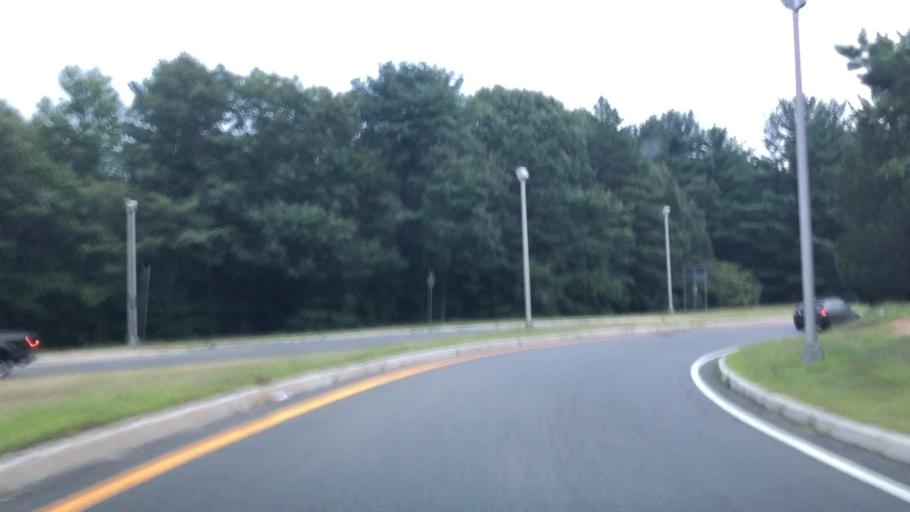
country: US
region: New Jersey
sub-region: Ocean County
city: Vista Center
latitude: 40.1609
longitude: -74.4227
